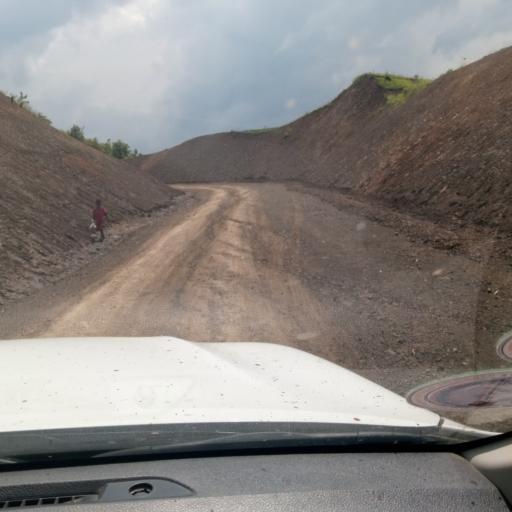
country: ET
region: Southern Nations, Nationalities, and People's Region
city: Arba Minch'
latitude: 6.3313
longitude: 37.3396
